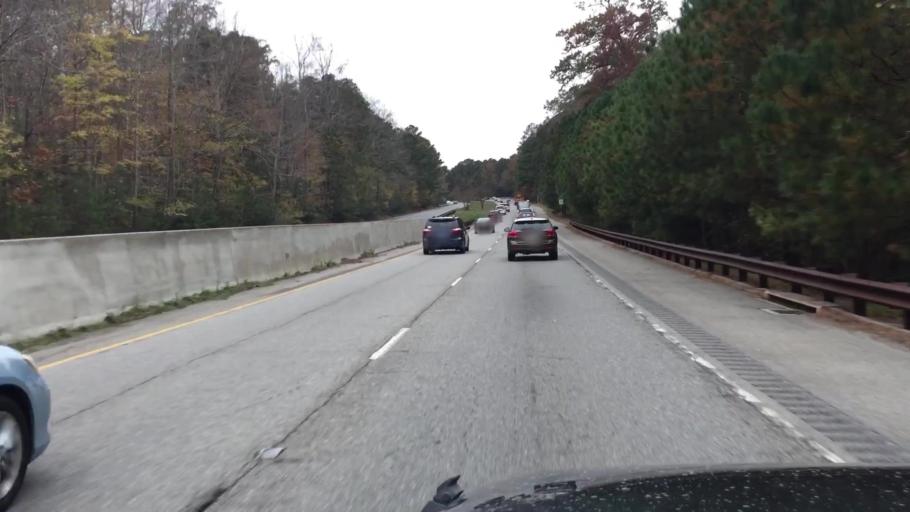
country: US
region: Virginia
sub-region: City of Williamsburg
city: Williamsburg
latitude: 37.2480
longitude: -76.6925
